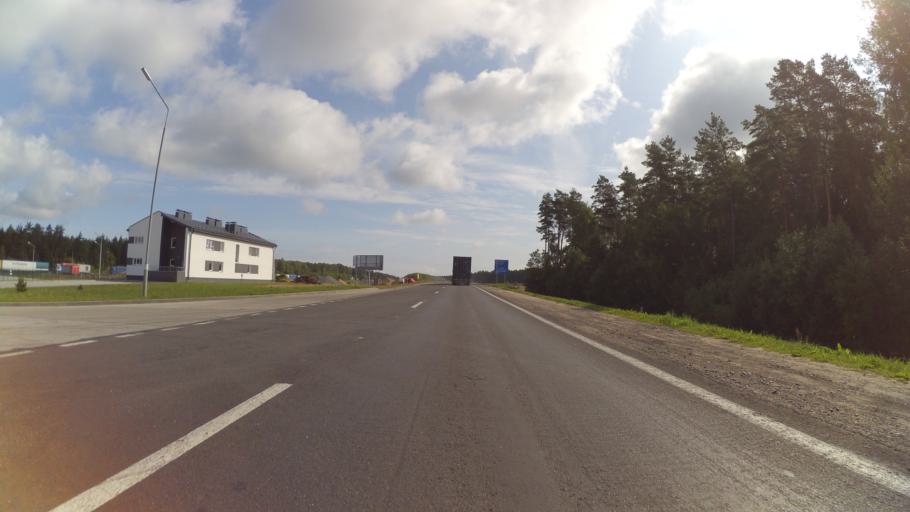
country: PL
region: Podlasie
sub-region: Powiat sokolski
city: Kuznica
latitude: 53.5281
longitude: 23.6784
